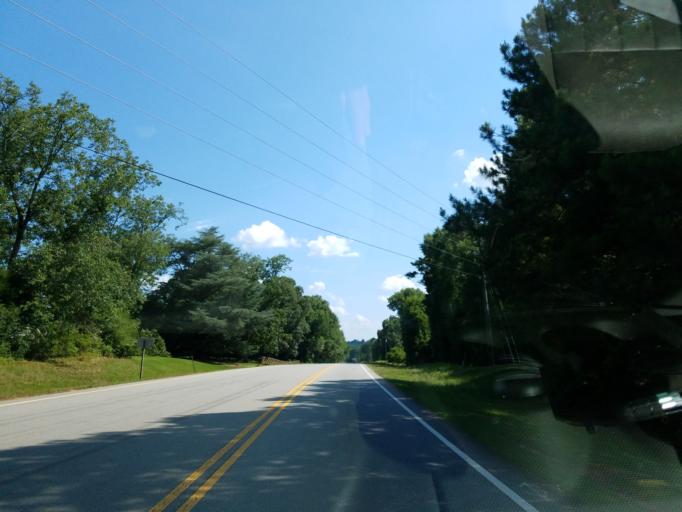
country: US
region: Georgia
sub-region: Lamar County
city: Barnesville
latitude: 32.9074
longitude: -84.0762
